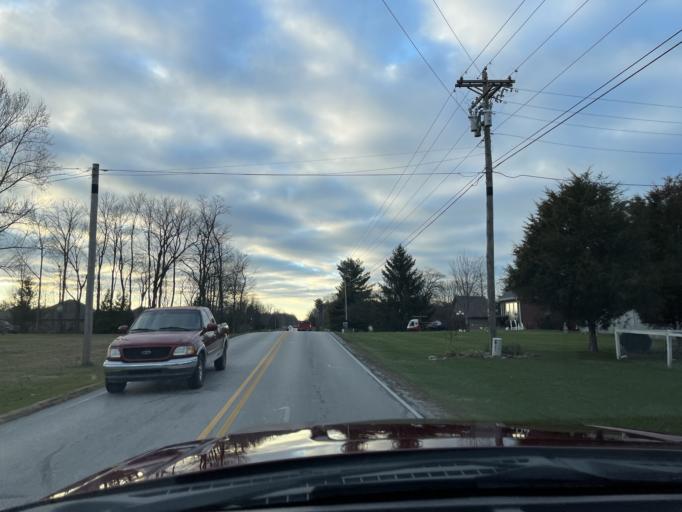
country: US
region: Indiana
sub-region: Hendricks County
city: Avon
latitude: 39.7773
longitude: -86.4049
